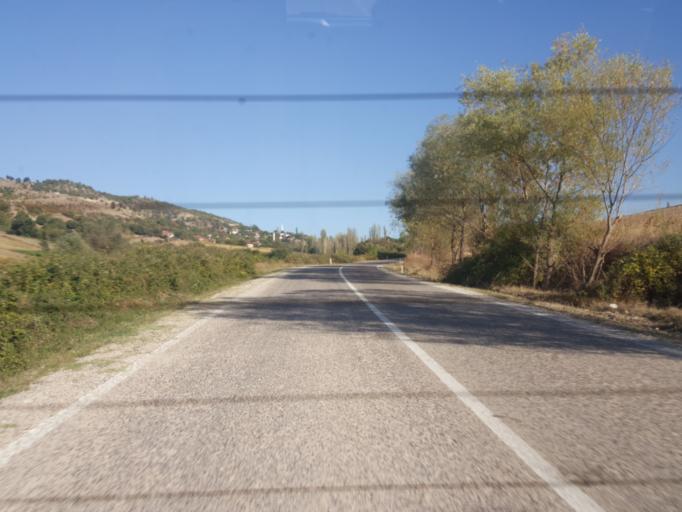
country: TR
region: Amasya
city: Tasova
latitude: 40.7167
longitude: 36.3142
